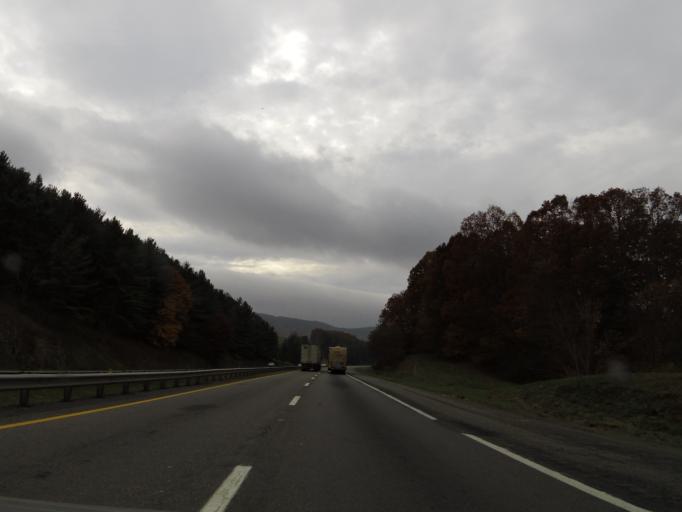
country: US
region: Virginia
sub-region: Bland County
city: Bland
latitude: 37.0702
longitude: -81.1268
